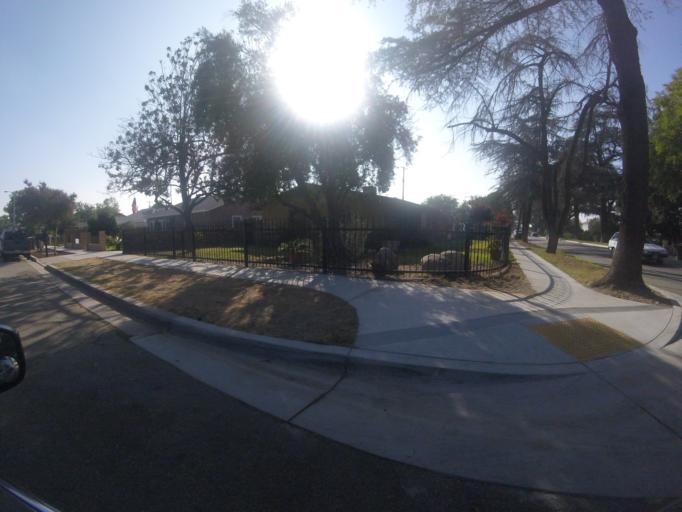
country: US
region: California
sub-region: San Bernardino County
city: Redlands
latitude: 34.0808
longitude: -117.1857
